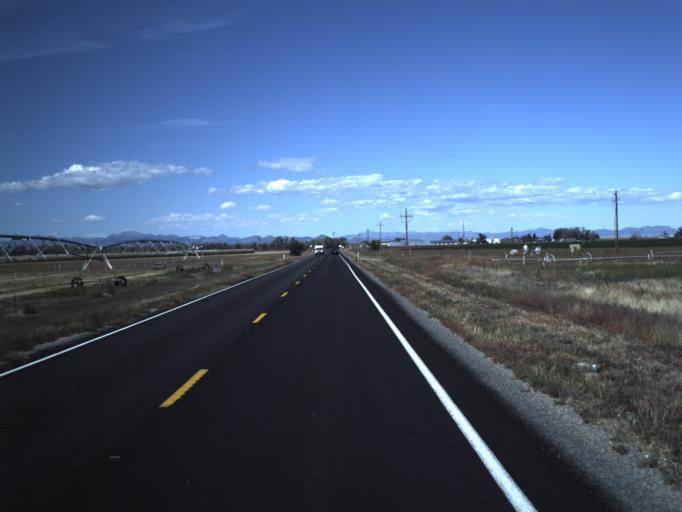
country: US
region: Utah
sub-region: Washington County
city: Enterprise
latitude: 37.6982
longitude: -113.6565
